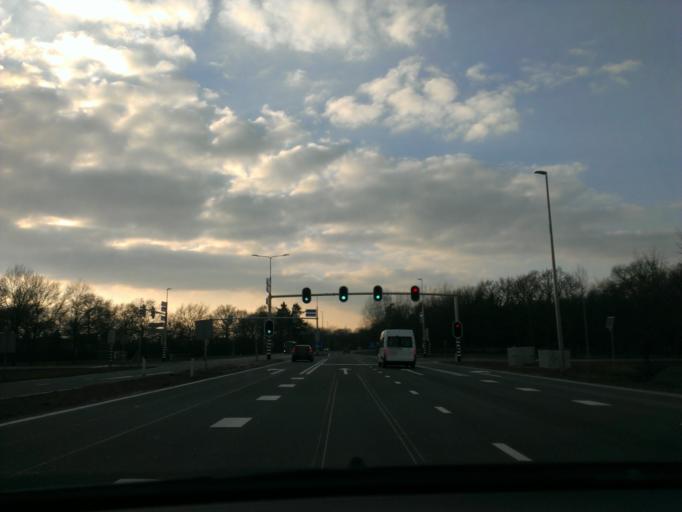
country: NL
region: Overijssel
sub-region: Gemeente Raalte
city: Heino
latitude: 52.4473
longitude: 6.2298
